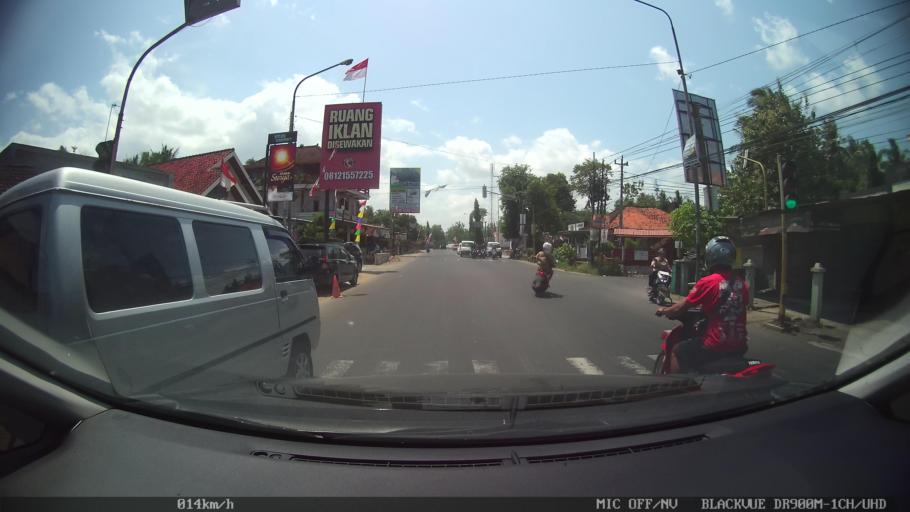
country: ID
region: Daerah Istimewa Yogyakarta
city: Bambanglipuro
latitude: -7.9309
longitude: 110.2726
